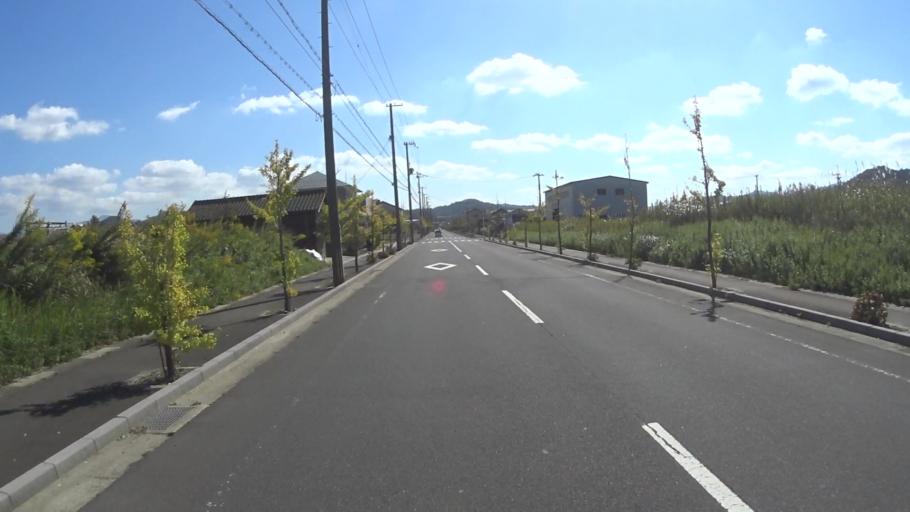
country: JP
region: Kyoto
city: Miyazu
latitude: 35.6822
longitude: 135.0203
